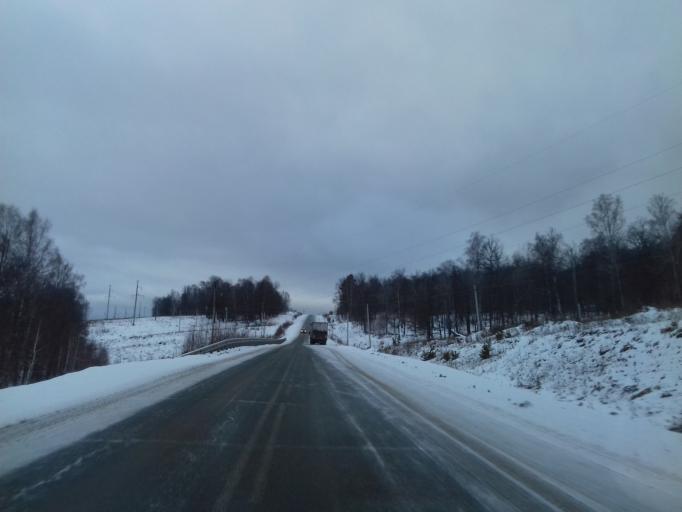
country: RU
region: Bashkortostan
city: Starosubkhangulovo
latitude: 53.2654
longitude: 57.5148
